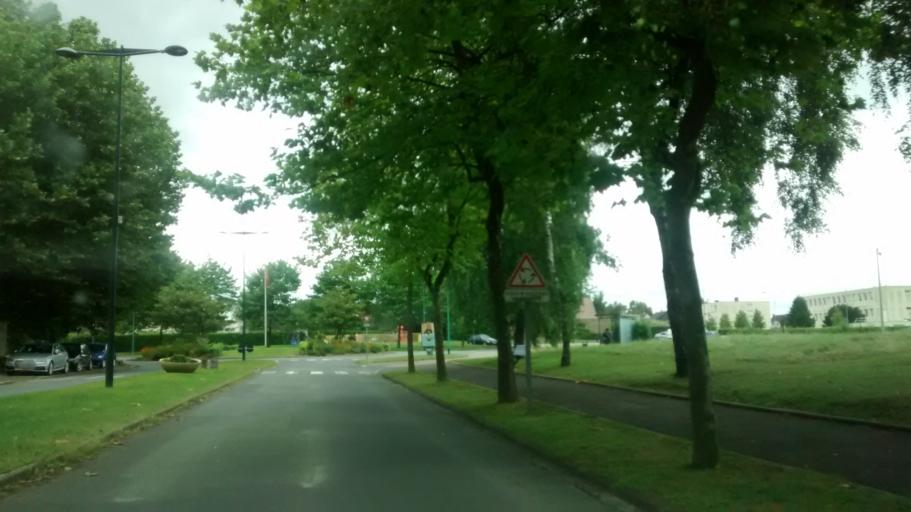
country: FR
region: Haute-Normandie
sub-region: Departement de la Seine-Maritime
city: Bois-Guillaume
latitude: 49.4696
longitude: 1.1414
